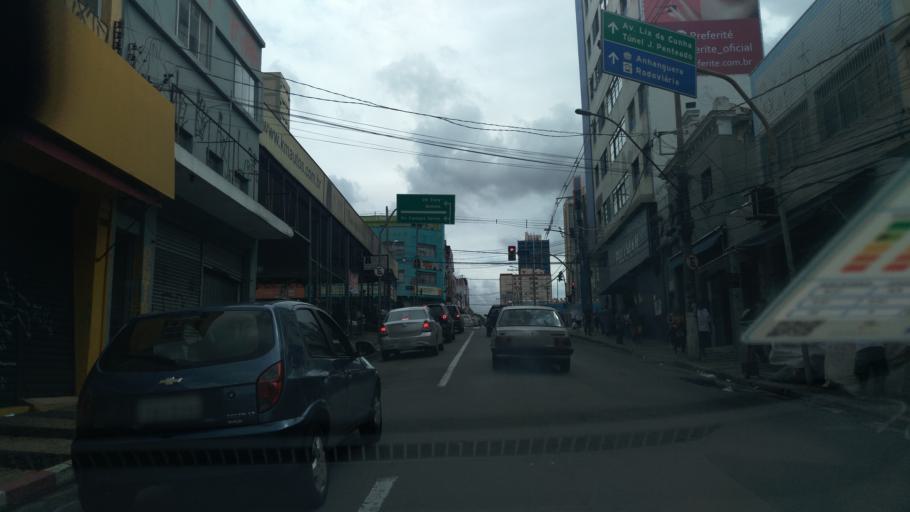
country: BR
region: Sao Paulo
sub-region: Campinas
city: Campinas
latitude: -22.9042
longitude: -47.0642
